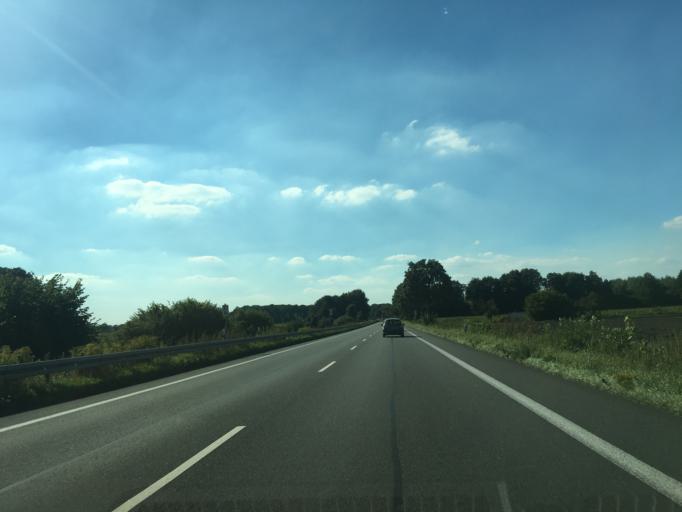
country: DE
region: North Rhine-Westphalia
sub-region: Regierungsbezirk Munster
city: Sassenberg
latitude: 51.9410
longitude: 8.0708
